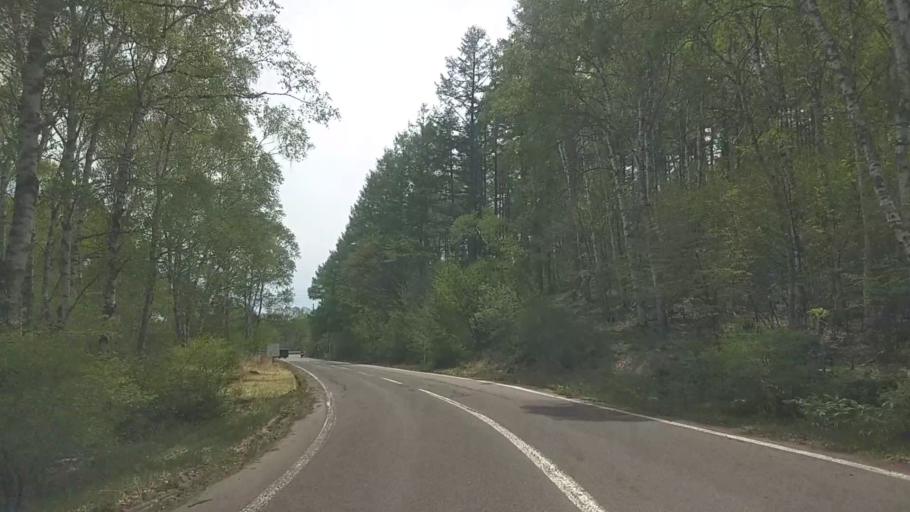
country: JP
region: Nagano
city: Saku
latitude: 36.0825
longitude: 138.3837
